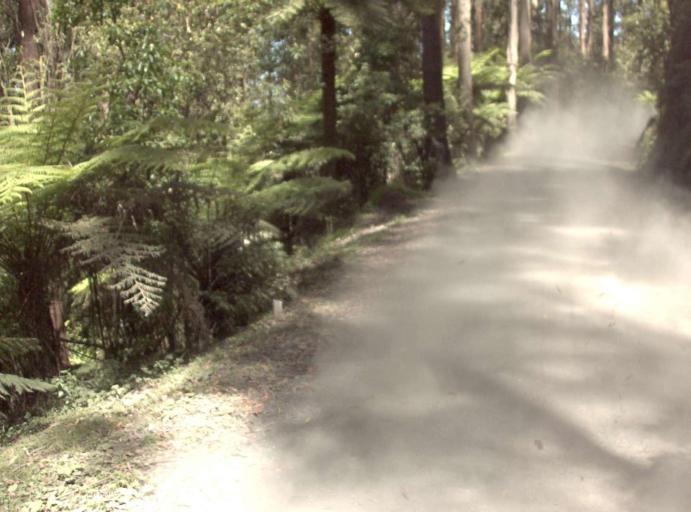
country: AU
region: Victoria
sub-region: Yarra Ranges
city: Millgrove
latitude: -37.6947
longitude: 145.7220
